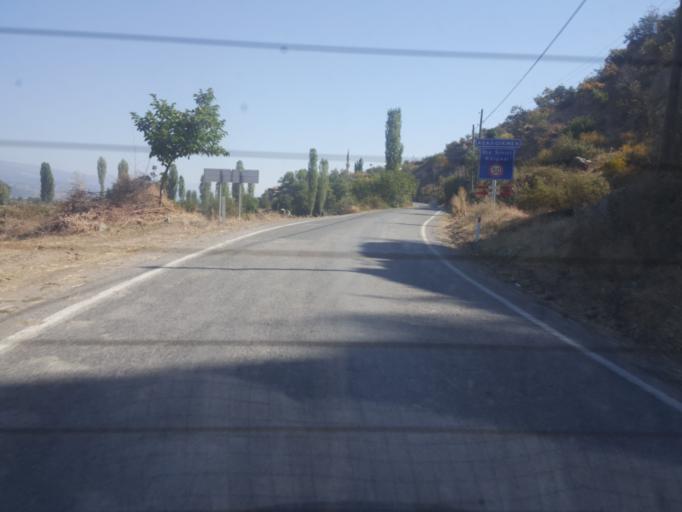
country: TR
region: Kastamonu
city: Tosya
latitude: 40.9852
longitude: 34.1018
